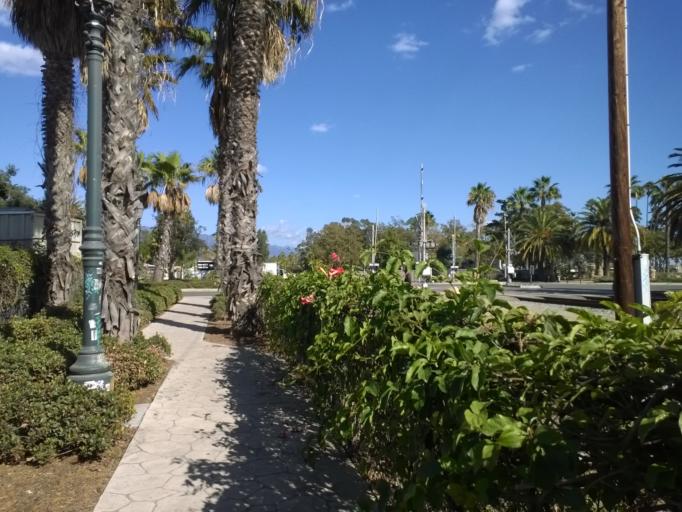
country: US
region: California
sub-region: Santa Barbara County
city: Santa Barbara
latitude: 34.4150
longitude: -119.6877
